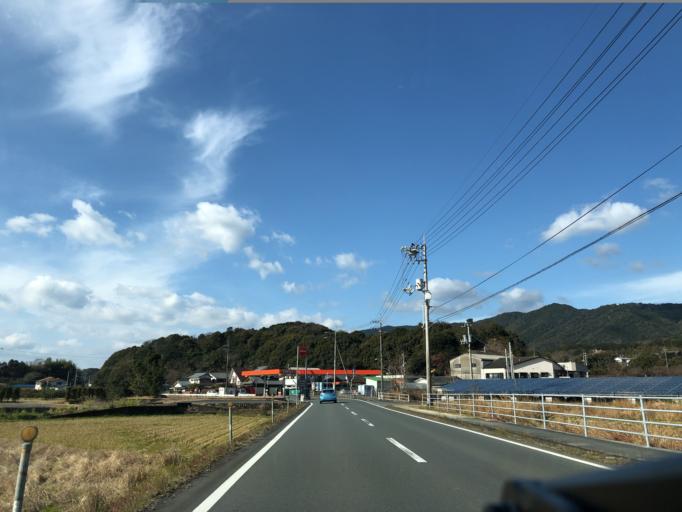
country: JP
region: Kochi
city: Sukumo
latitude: 32.9304
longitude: 132.6948
